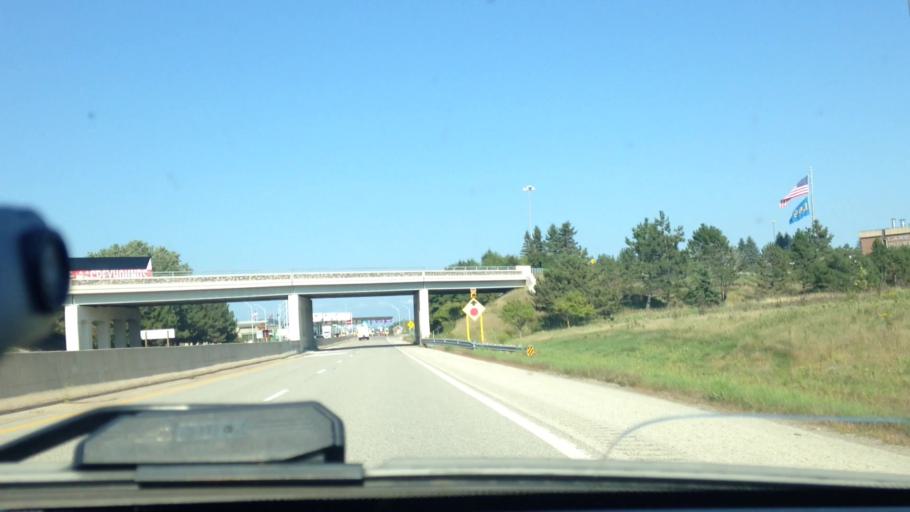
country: US
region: Michigan
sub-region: Chippewa County
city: Sault Ste. Marie
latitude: 46.4909
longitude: -84.3718
